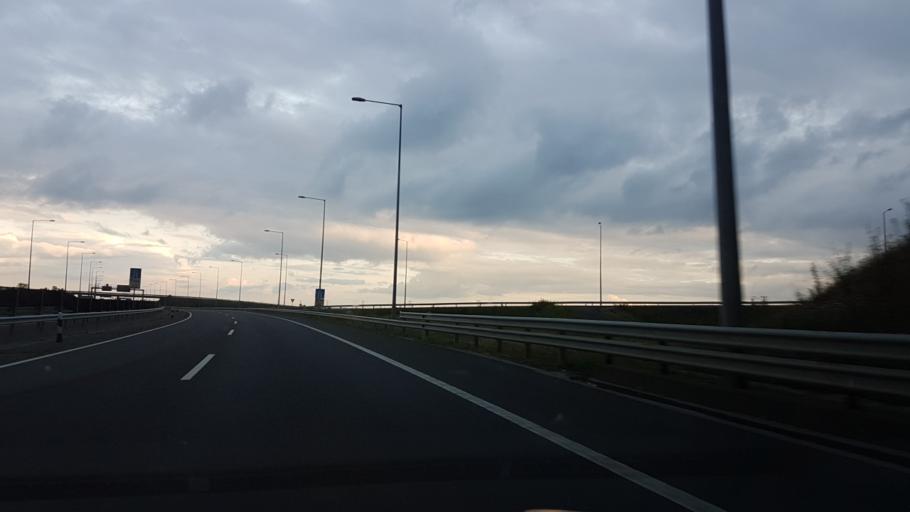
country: HU
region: Borsod-Abauj-Zemplen
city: Alsozsolca
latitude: 48.0604
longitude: 20.8448
